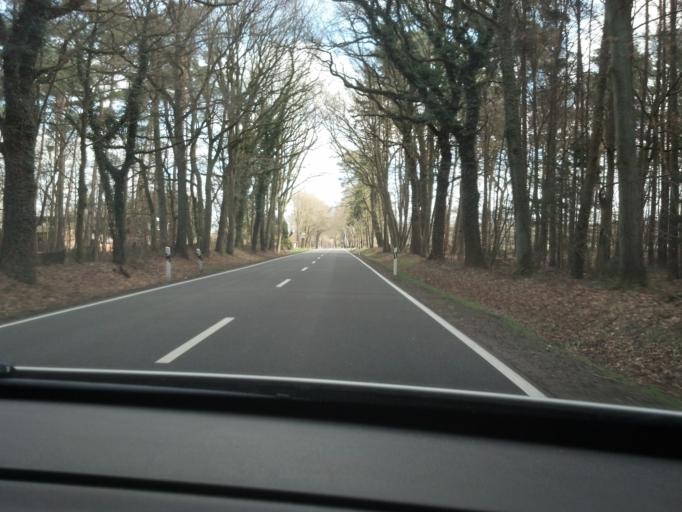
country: DE
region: Schleswig-Holstein
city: Langenlehsten
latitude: 53.4451
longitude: 10.7596
